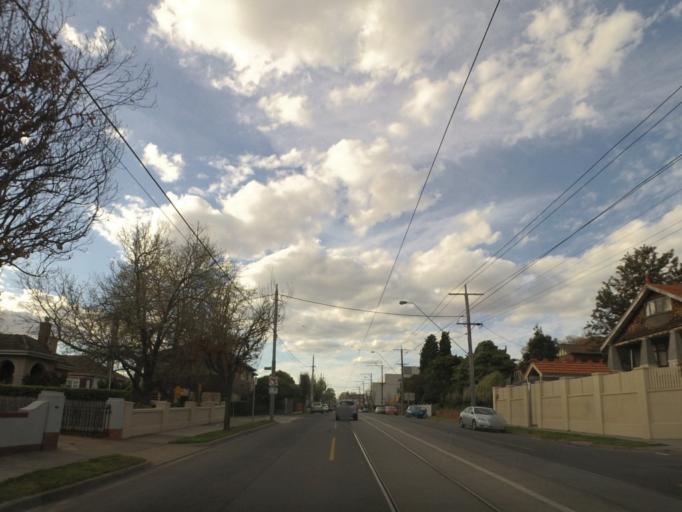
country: AU
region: Victoria
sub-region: Stonnington
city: Glen Iris
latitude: -37.8476
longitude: 145.0535
